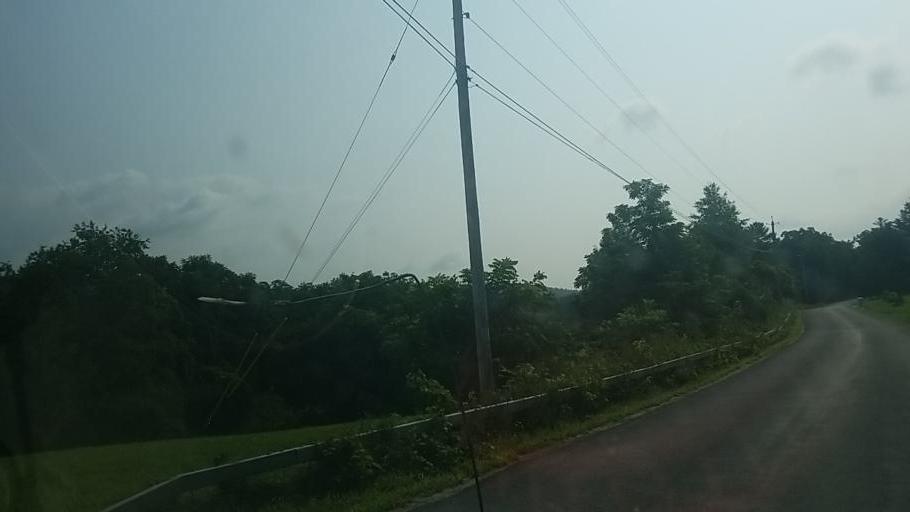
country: US
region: New York
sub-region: Montgomery County
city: Fonda
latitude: 42.9691
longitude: -74.4267
